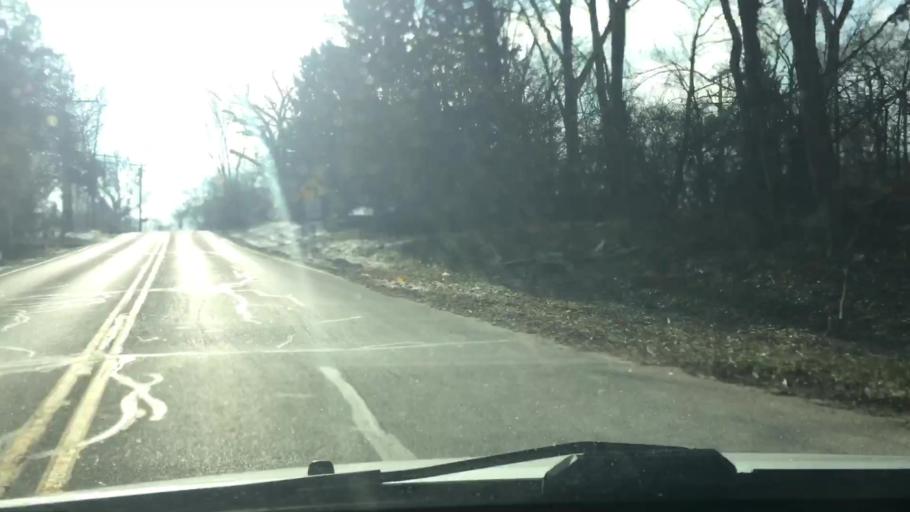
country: US
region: Wisconsin
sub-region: Waukesha County
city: Waukesha
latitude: 42.9884
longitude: -88.2888
